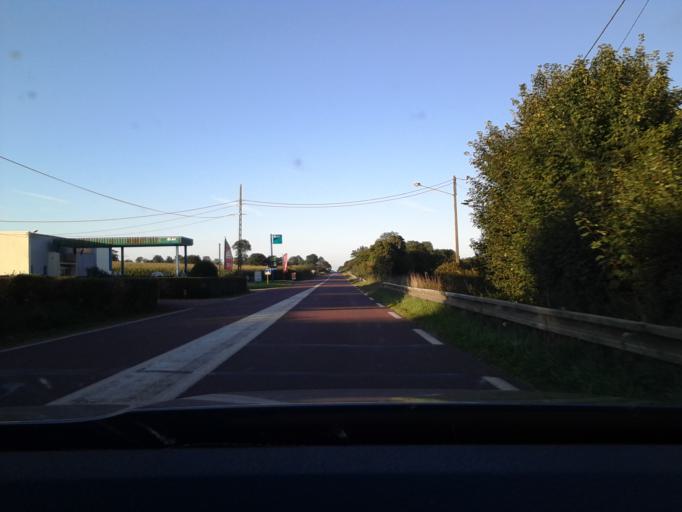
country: FR
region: Lower Normandy
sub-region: Departement de la Manche
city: Valognes
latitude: 49.4590
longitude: -1.4914
